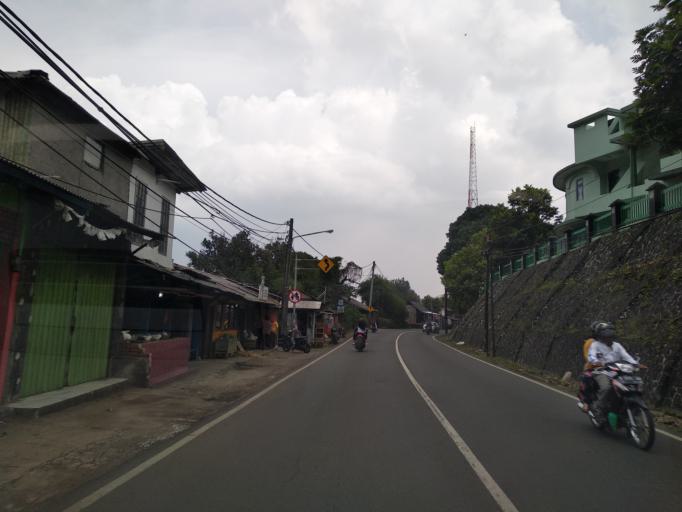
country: ID
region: West Java
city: Lembang
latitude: -6.8250
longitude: 107.6096
